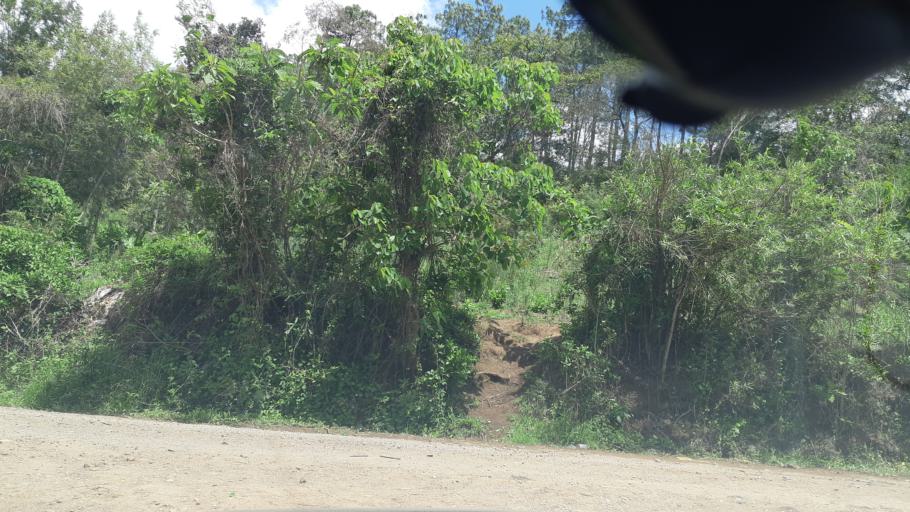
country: GT
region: Chimaltenango
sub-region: Municipio de Chimaltenango
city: Chimaltenango
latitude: 14.6520
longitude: -90.8482
